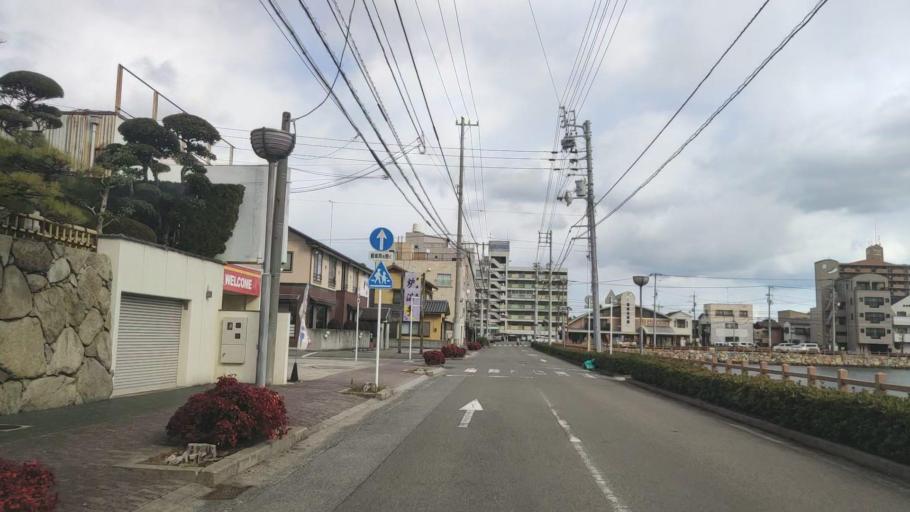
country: JP
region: Ehime
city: Saijo
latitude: 34.0647
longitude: 133.0064
